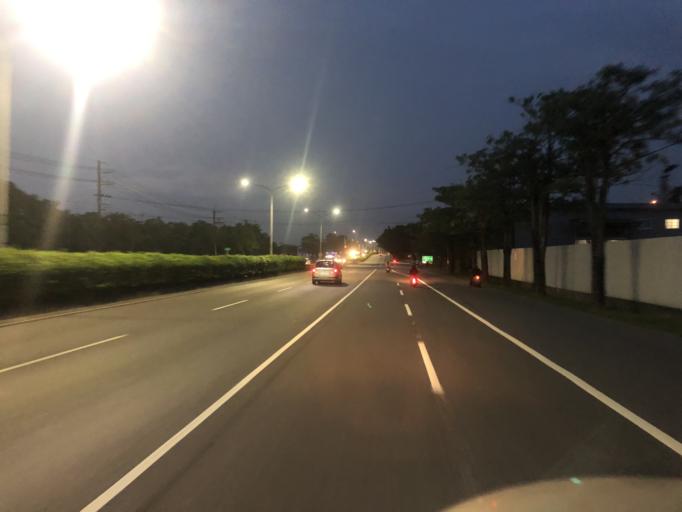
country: TW
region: Taiwan
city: Yujing
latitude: 23.1670
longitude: 120.3404
